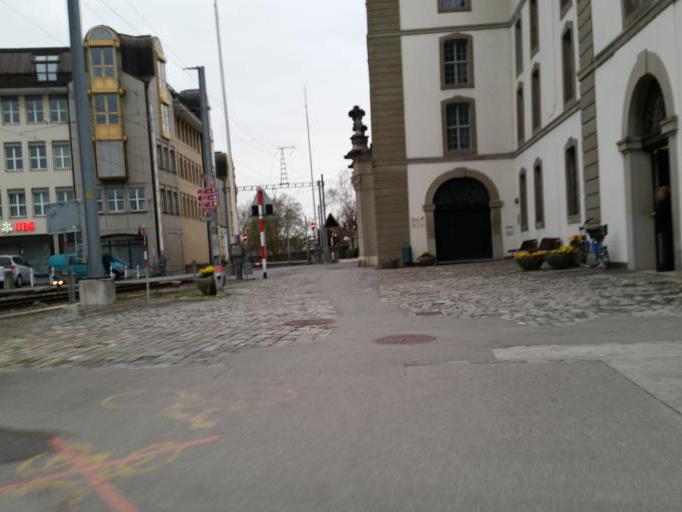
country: CH
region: Saint Gallen
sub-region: Wahlkreis Rorschach
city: Rorschach
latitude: 47.4791
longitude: 9.4922
